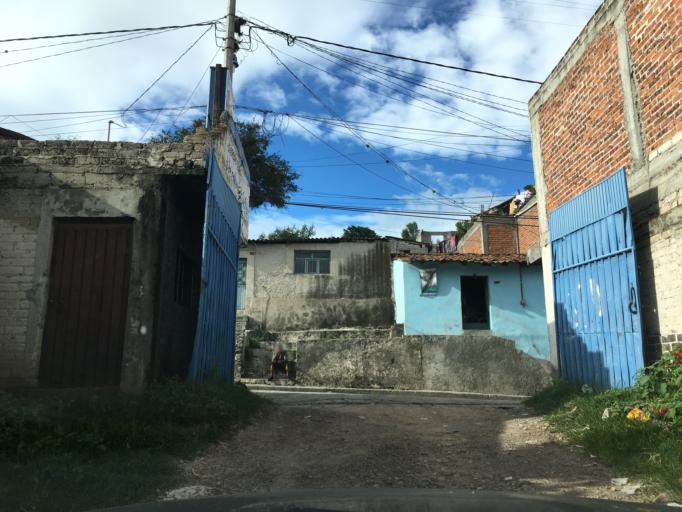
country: MX
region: Guanajuato
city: Iramuco
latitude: 19.9576
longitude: -100.9305
